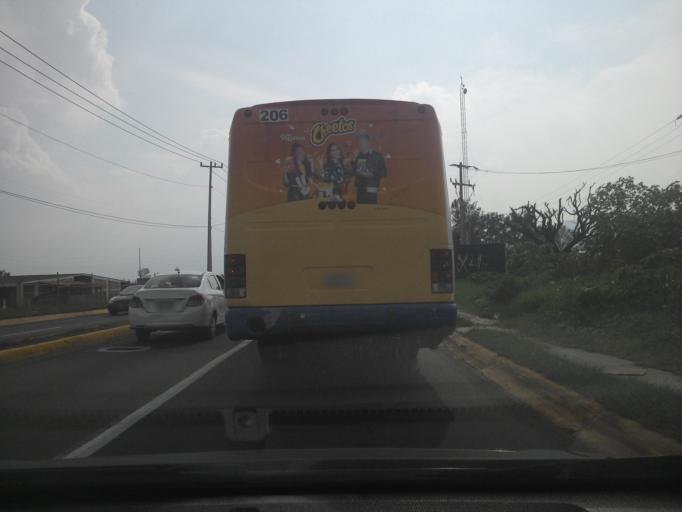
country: MX
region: Jalisco
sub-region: San Pedro Tlaquepaque
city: Paseo del Prado
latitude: 20.5508
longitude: -103.4006
